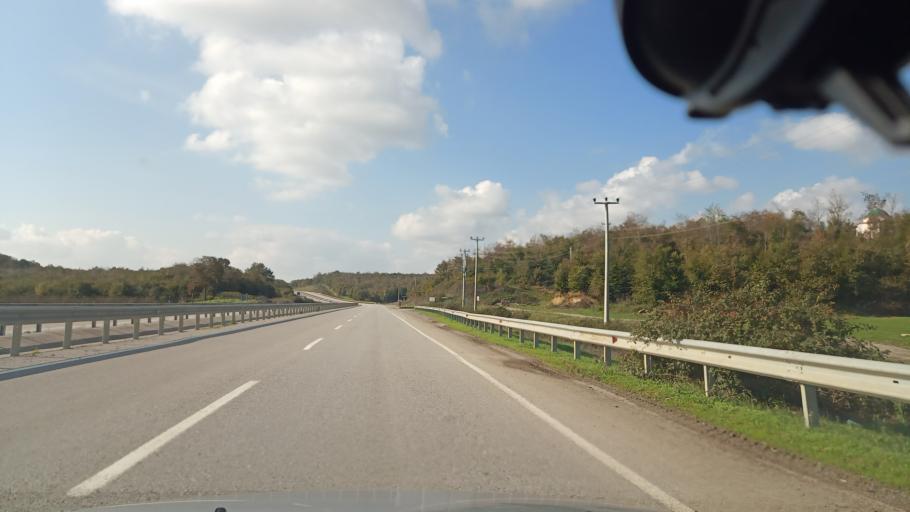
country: TR
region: Sakarya
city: Kaynarca
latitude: 41.0708
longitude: 30.3699
